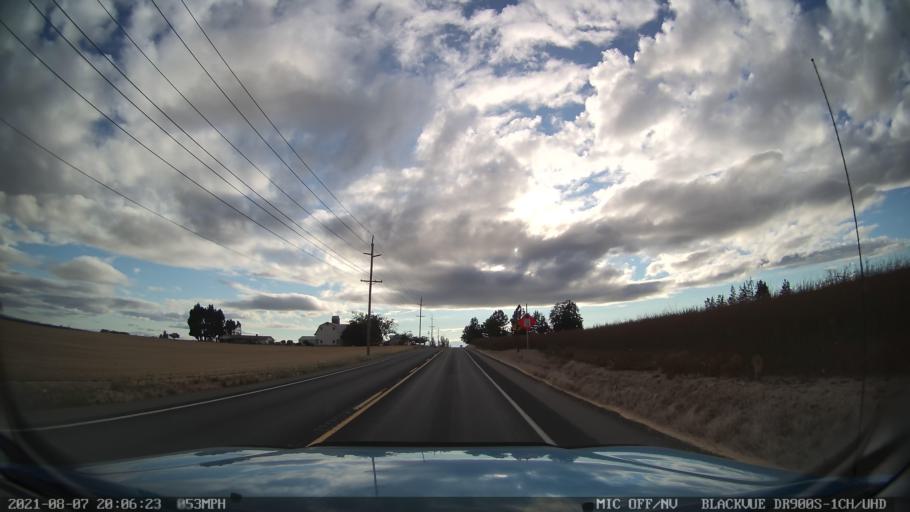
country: US
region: Oregon
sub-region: Marion County
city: Silverton
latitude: 44.9914
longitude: -122.8674
